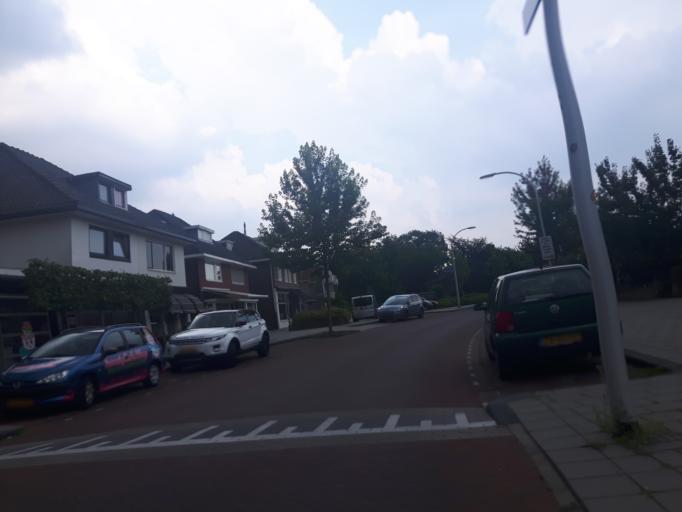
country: NL
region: Overijssel
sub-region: Gemeente Hengelo
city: Hengelo
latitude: 52.2755
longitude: 6.7871
